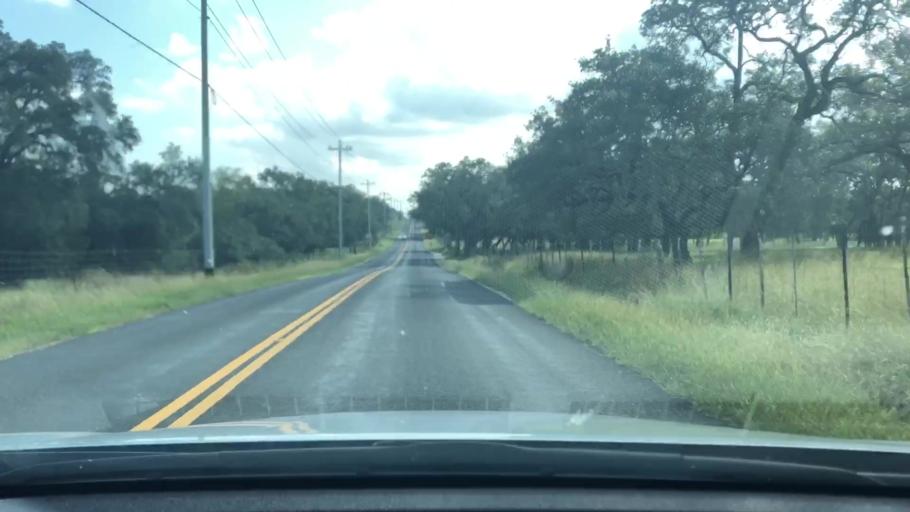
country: US
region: Texas
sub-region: Bexar County
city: Fair Oaks Ranch
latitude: 29.7837
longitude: -98.6267
